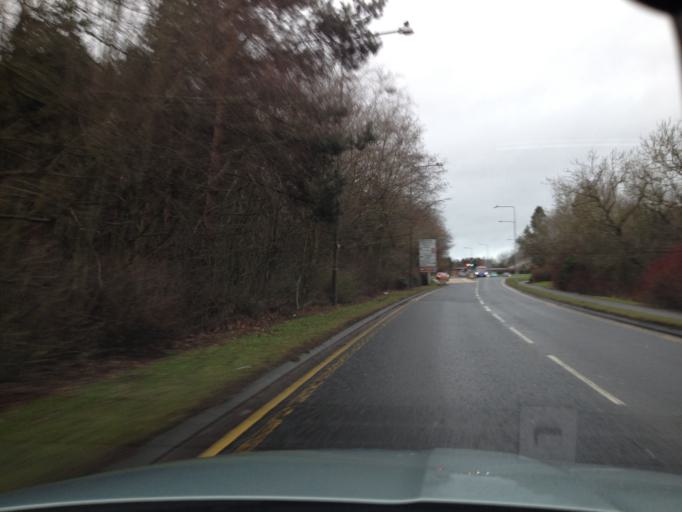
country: GB
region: Scotland
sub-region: West Lothian
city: Livingston
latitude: 55.8892
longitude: -3.5263
